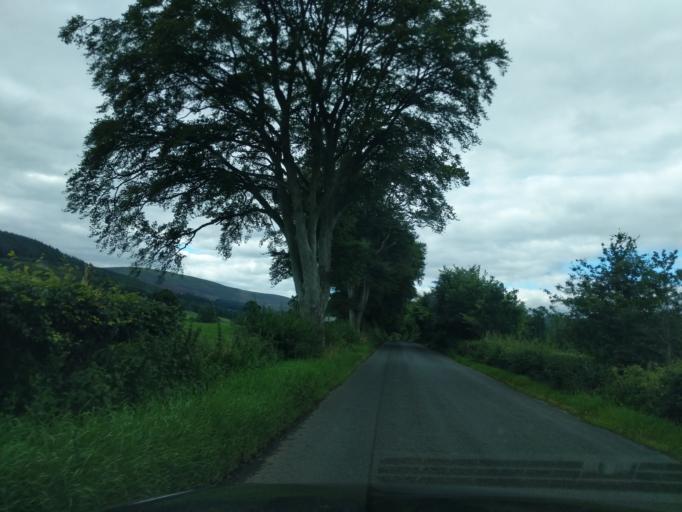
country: GB
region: Scotland
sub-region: The Scottish Borders
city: Peebles
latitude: 55.6297
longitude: -3.2922
